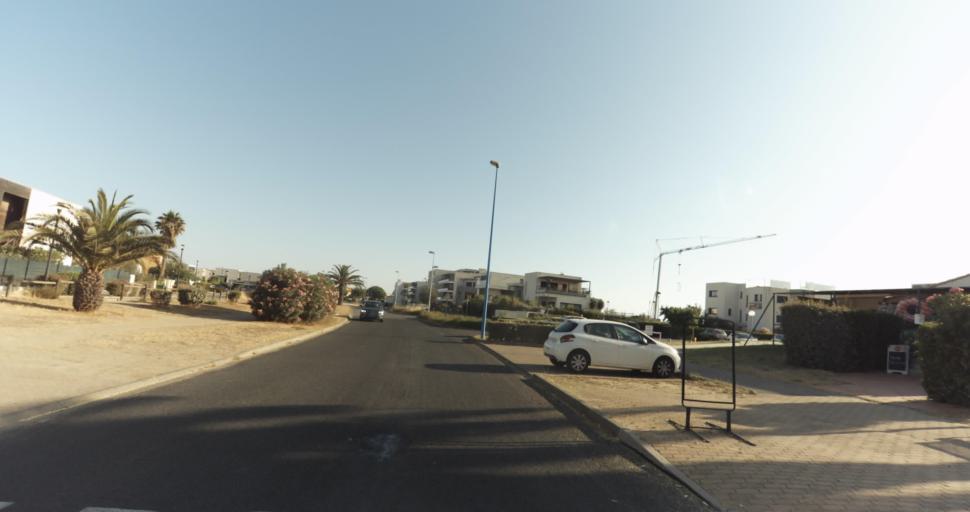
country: FR
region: Languedoc-Roussillon
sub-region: Departement des Pyrenees-Orientales
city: Saint-Cyprien-Plage
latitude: 42.6025
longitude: 3.0401
